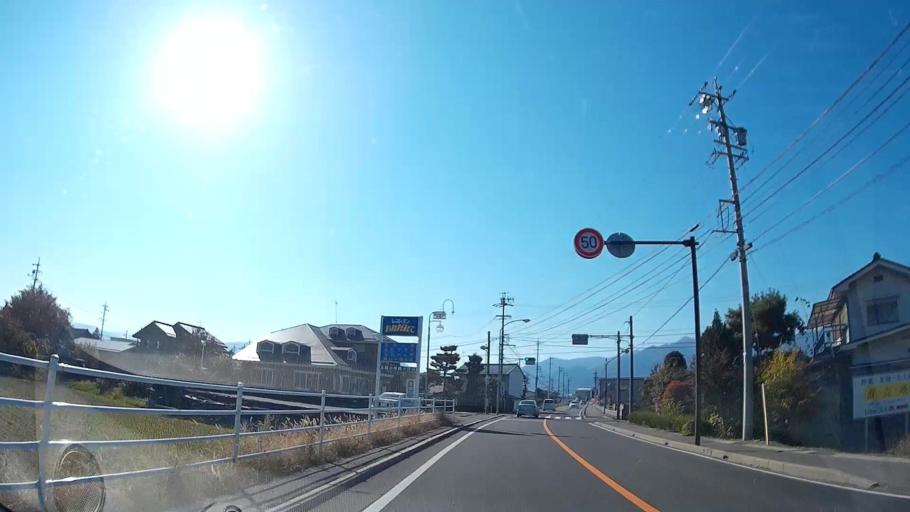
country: JP
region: Nagano
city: Matsumoto
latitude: 36.2241
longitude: 137.9153
